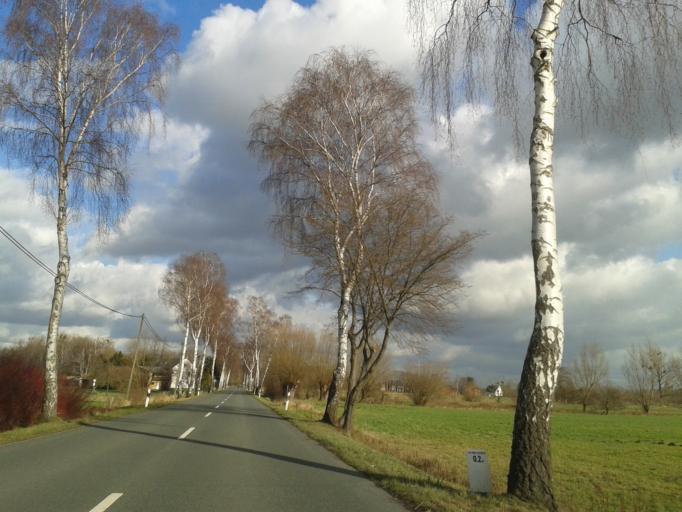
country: DE
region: North Rhine-Westphalia
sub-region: Regierungsbezirk Detmold
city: Salzkotten
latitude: 51.6890
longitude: 8.5727
